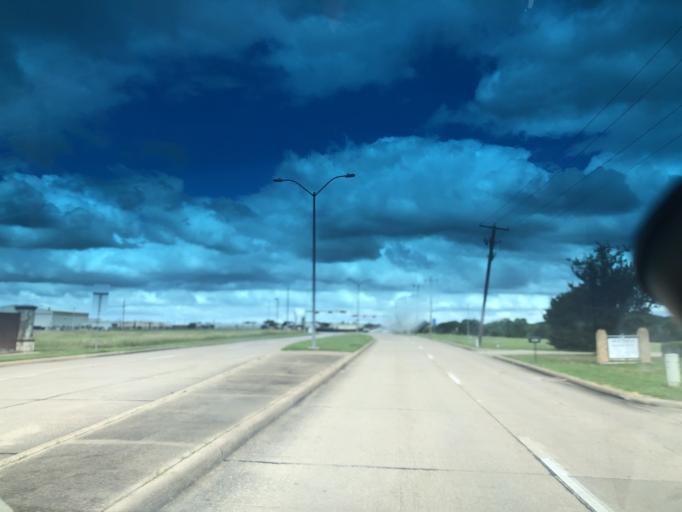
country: US
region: Texas
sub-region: Dallas County
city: Grand Prairie
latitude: 32.7062
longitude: -97.0422
